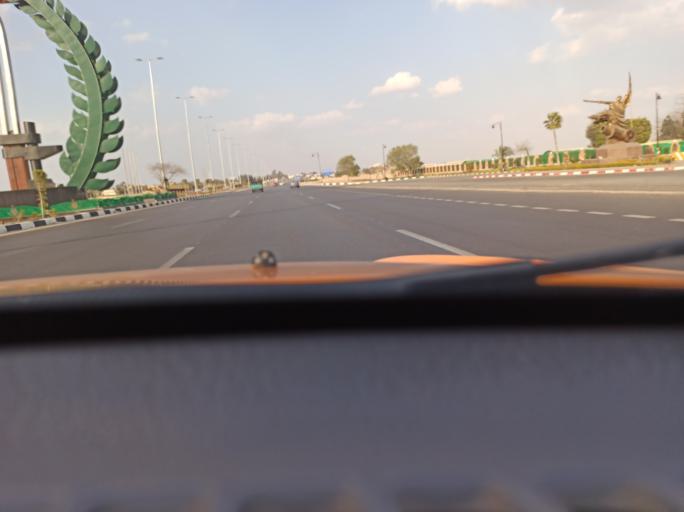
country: EG
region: Al Isma'iliyah
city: Ismailia
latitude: 30.6072
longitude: 32.2146
